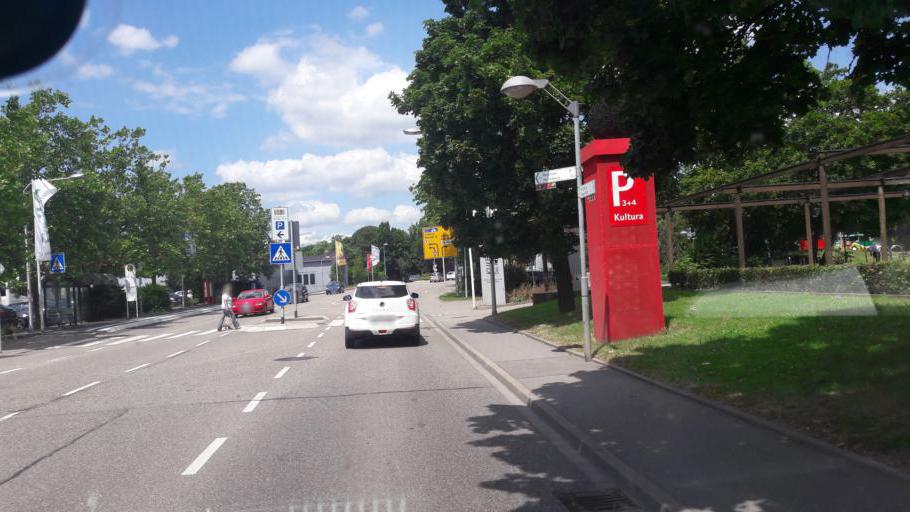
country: DE
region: Baden-Wuerttemberg
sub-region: Regierungsbezirk Stuttgart
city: Ohringen
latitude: 49.2003
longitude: 9.4970
